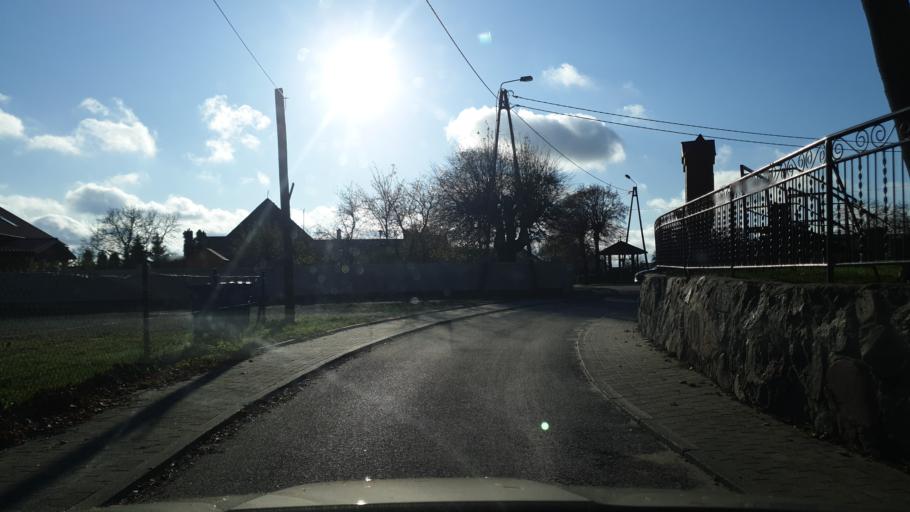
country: PL
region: Pomeranian Voivodeship
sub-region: Powiat pucki
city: Gniezdzewo
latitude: 54.7600
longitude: 18.4005
